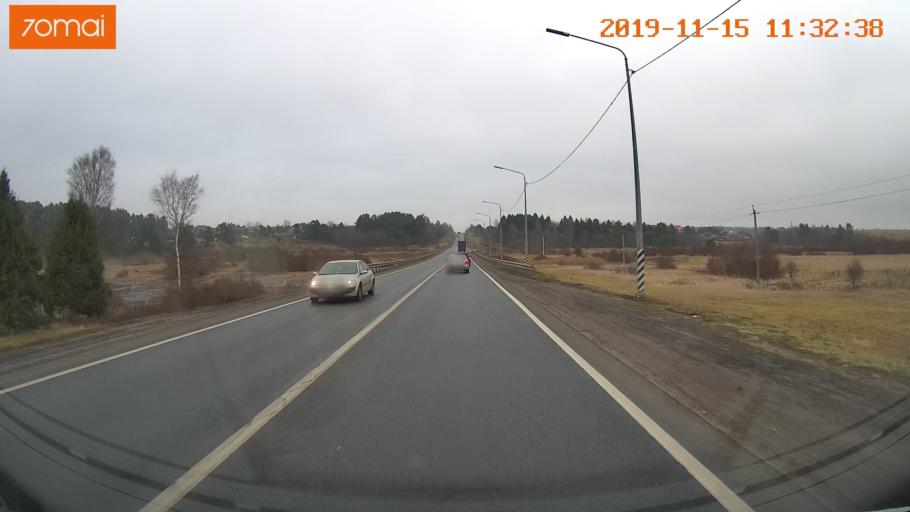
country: RU
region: Vologda
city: Molochnoye
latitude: 59.1864
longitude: 39.5782
